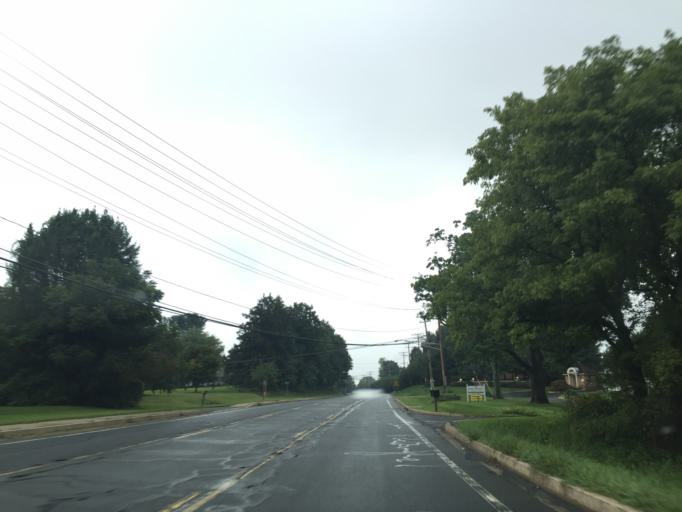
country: US
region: Maryland
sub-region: Harford County
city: Bel Air South
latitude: 39.5080
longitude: -76.3282
